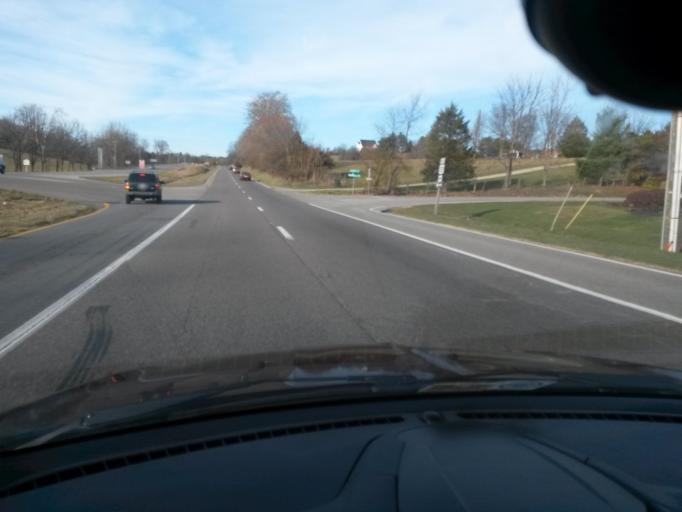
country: US
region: Virginia
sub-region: Botetourt County
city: Daleville
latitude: 37.4373
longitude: -79.9033
